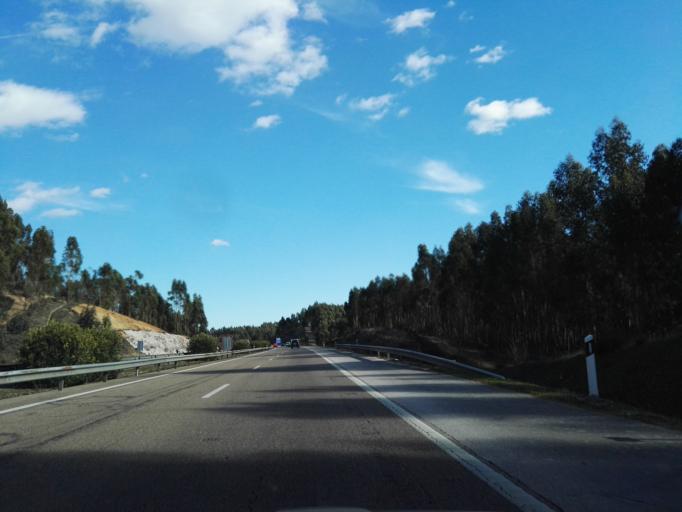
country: PT
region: Santarem
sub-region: Chamusca
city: Vila Nova da Barquinha
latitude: 39.4866
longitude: -8.4184
